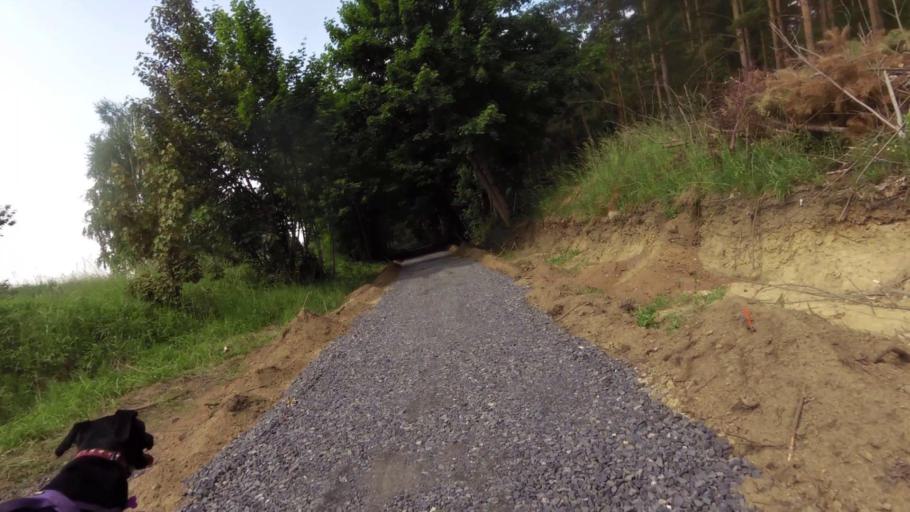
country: PL
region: West Pomeranian Voivodeship
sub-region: Powiat pyrzycki
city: Bielice
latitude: 53.2031
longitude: 14.6175
